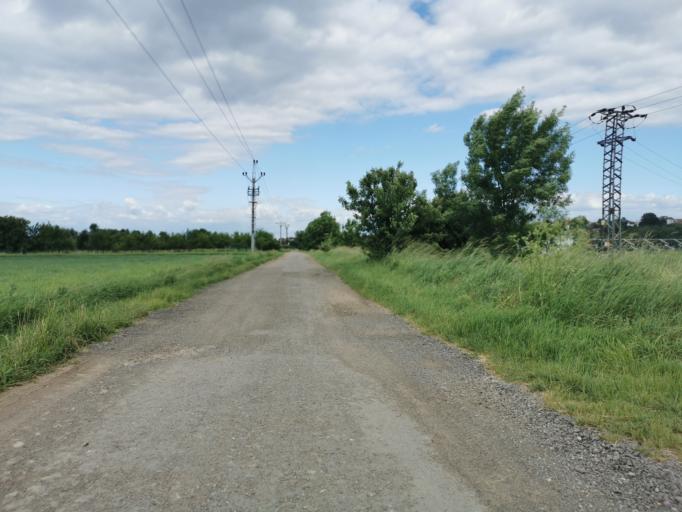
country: CZ
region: South Moravian
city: Vnorovy
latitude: 48.9297
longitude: 17.3350
